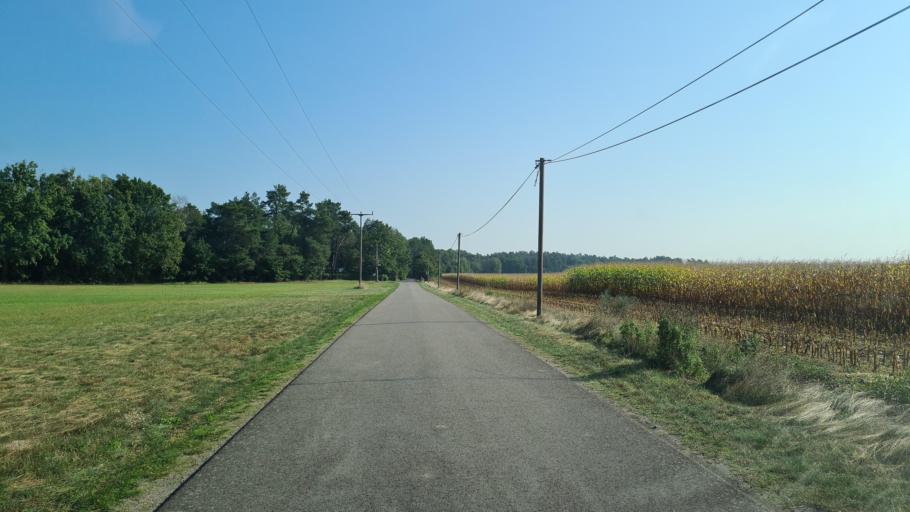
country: DE
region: Brandenburg
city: Luckau
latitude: 51.7785
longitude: 13.7003
